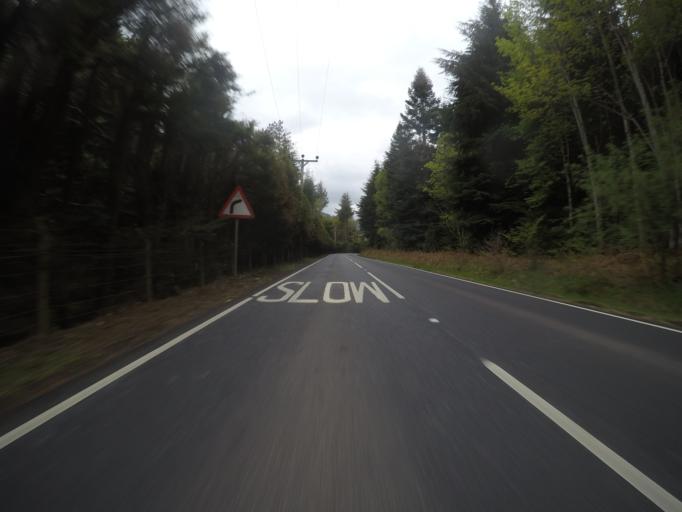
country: GB
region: Scotland
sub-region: Highland
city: Beauly
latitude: 57.1887
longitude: -4.6192
